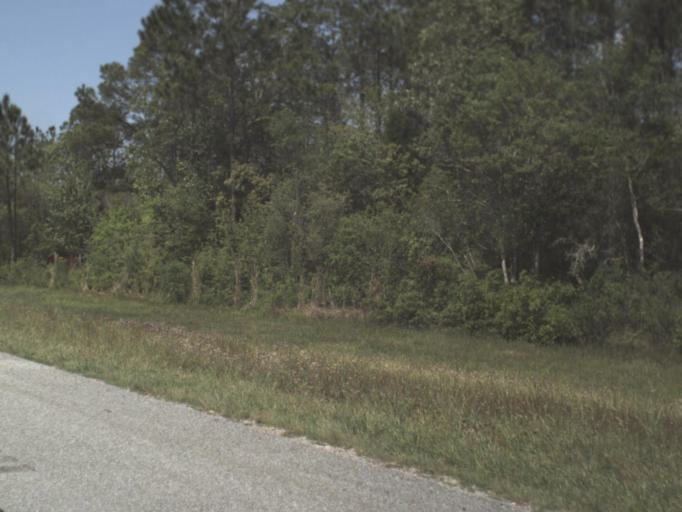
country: US
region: Florida
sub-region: Santa Rosa County
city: Bagdad
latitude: 30.5607
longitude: -87.0436
